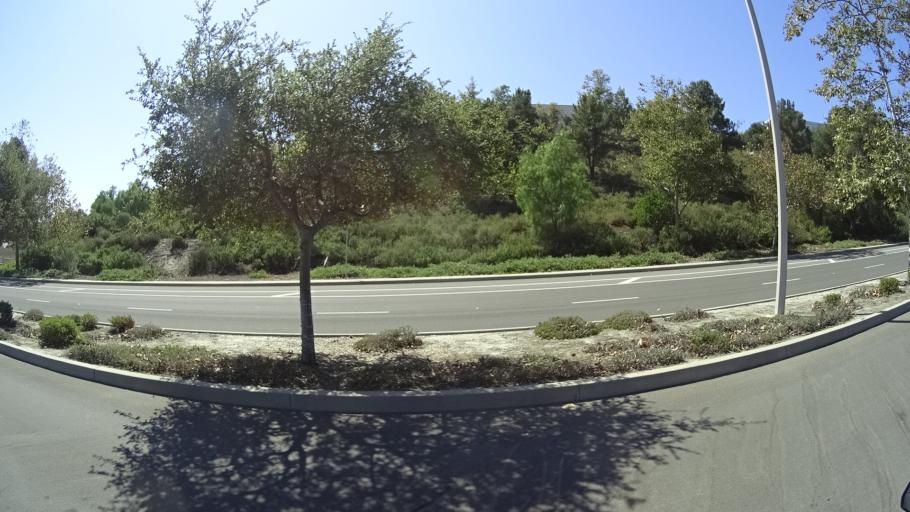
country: US
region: California
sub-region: Orange County
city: San Clemente
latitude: 33.4465
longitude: -117.5857
